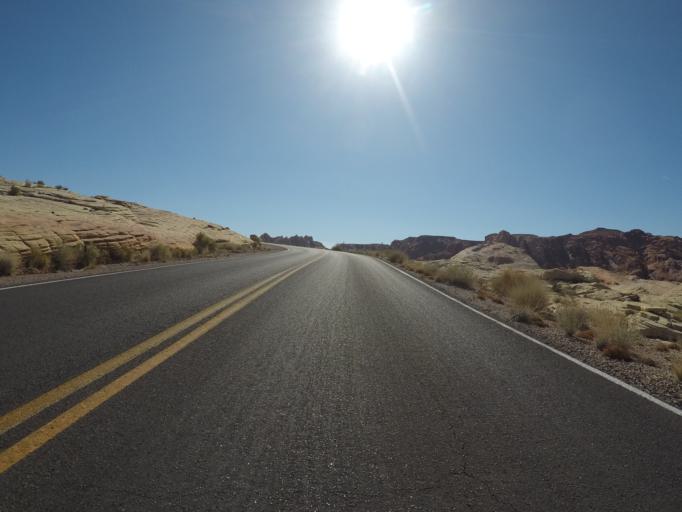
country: US
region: Nevada
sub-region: Clark County
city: Moapa Valley
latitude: 36.4654
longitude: -114.5242
